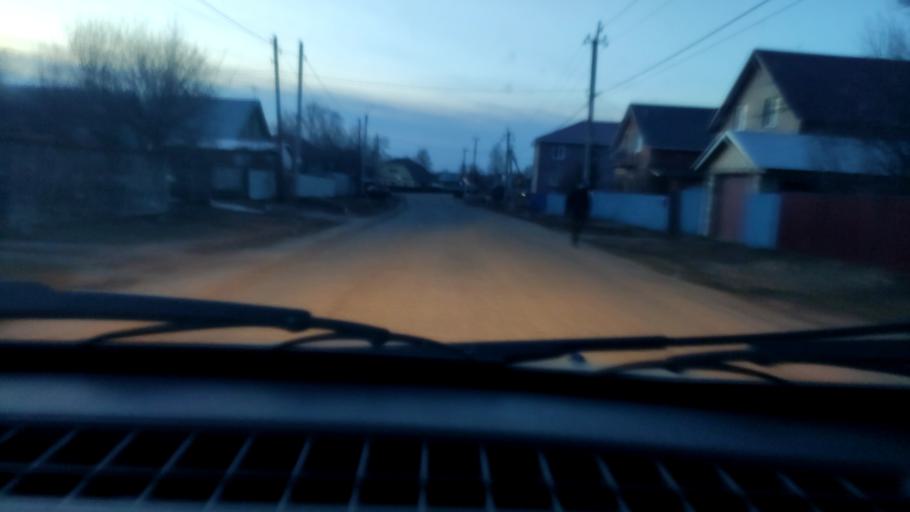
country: RU
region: Bashkortostan
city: Iglino
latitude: 54.8136
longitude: 56.3918
